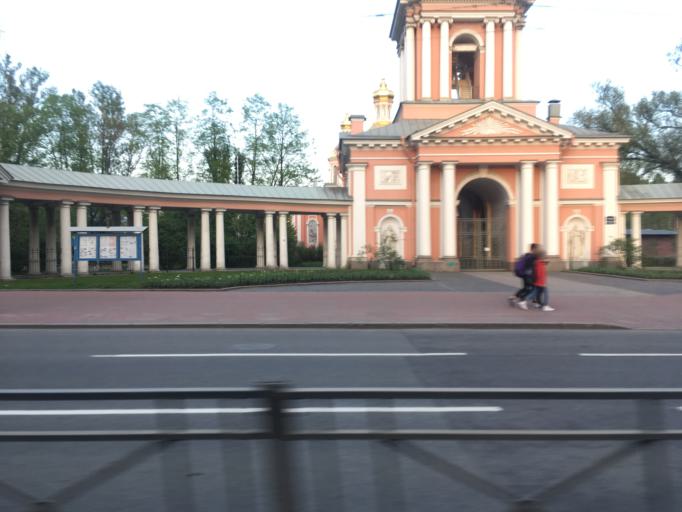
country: RU
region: St.-Petersburg
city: Centralniy
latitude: 59.9167
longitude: 30.3518
